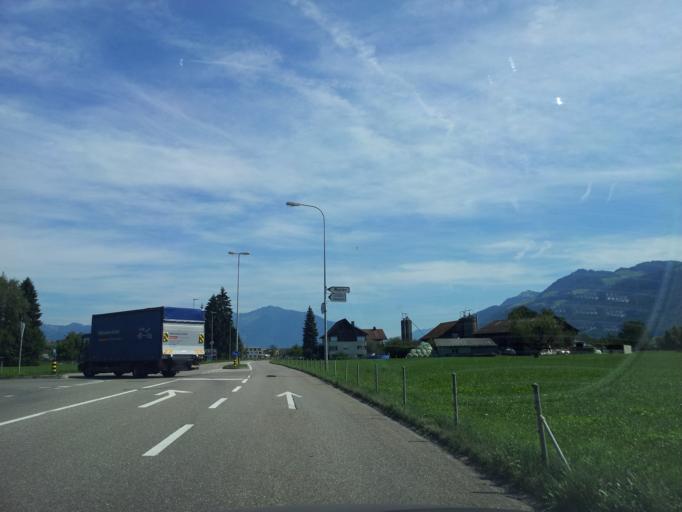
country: CH
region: Schwyz
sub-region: Bezirk March
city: Lachen
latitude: 47.1919
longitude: 8.8822
